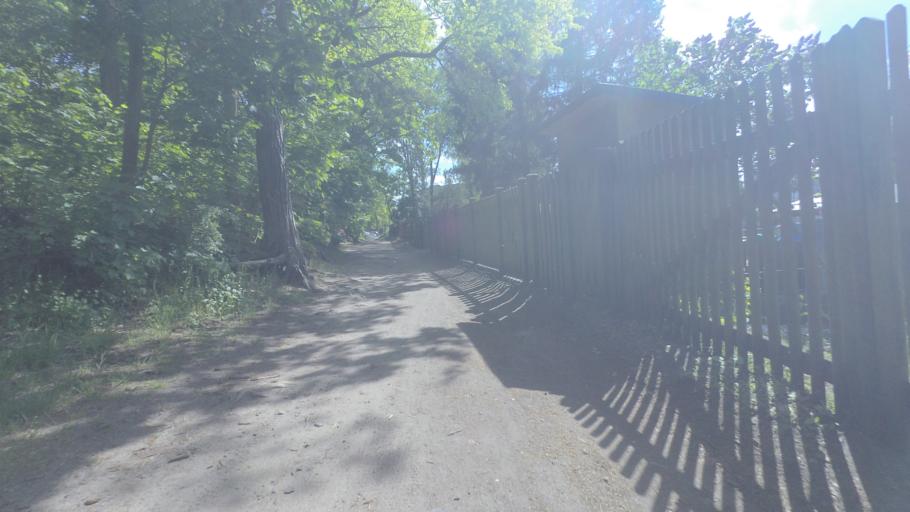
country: DE
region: Brandenburg
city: Erkner
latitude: 52.4227
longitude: 13.7636
